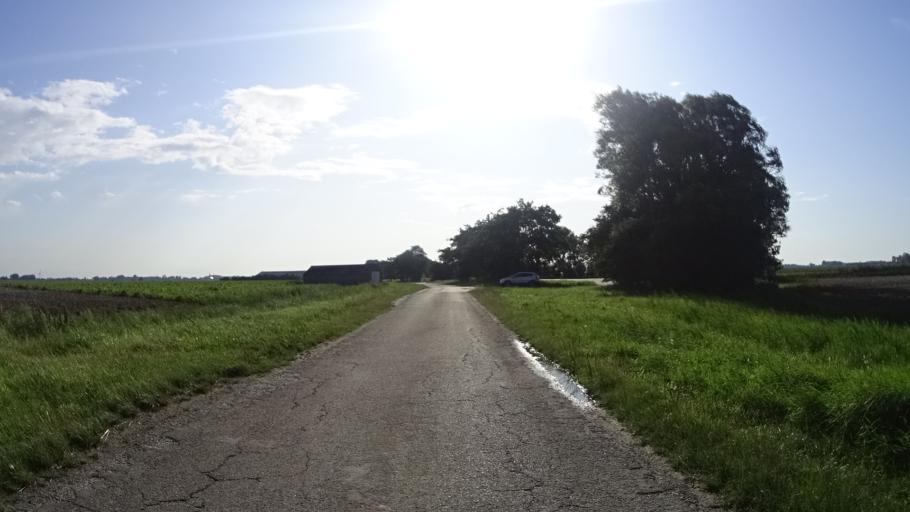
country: NL
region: Friesland
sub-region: Gemeente Harlingen
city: Harlingen
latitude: 53.1229
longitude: 5.4394
